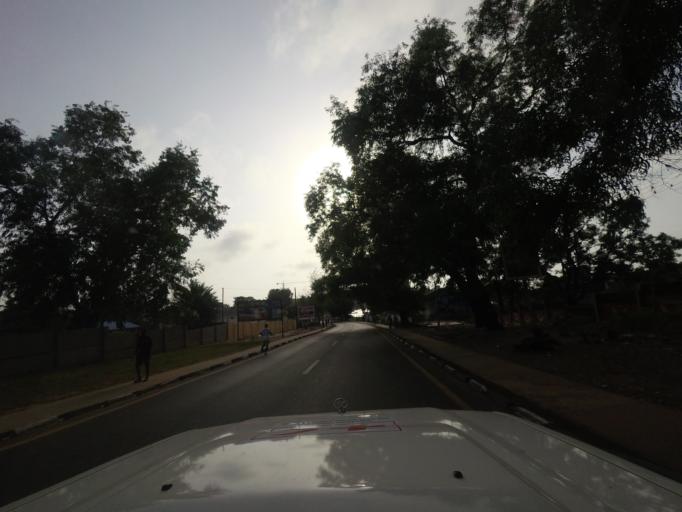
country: SL
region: Western Area
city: Freetown
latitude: 8.4935
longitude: -13.2905
